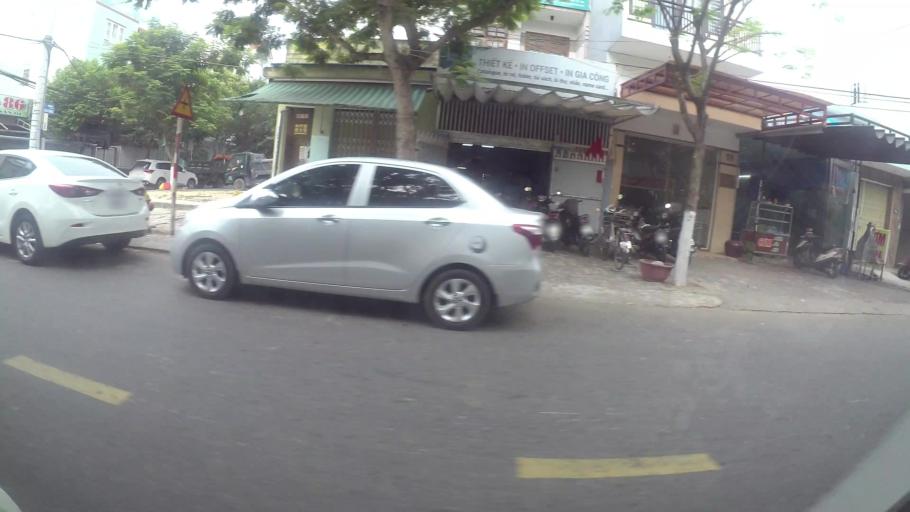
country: VN
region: Da Nang
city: Son Tra
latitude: 16.0514
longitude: 108.2401
